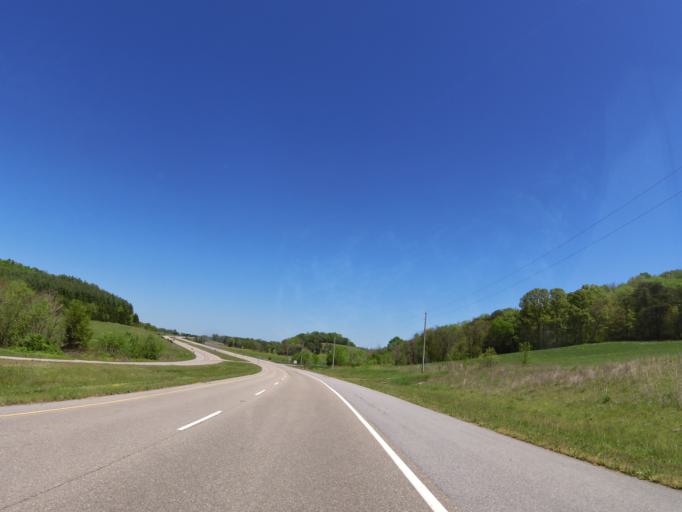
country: US
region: Tennessee
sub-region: Cocke County
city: Newport
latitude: 36.0218
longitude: -83.0367
